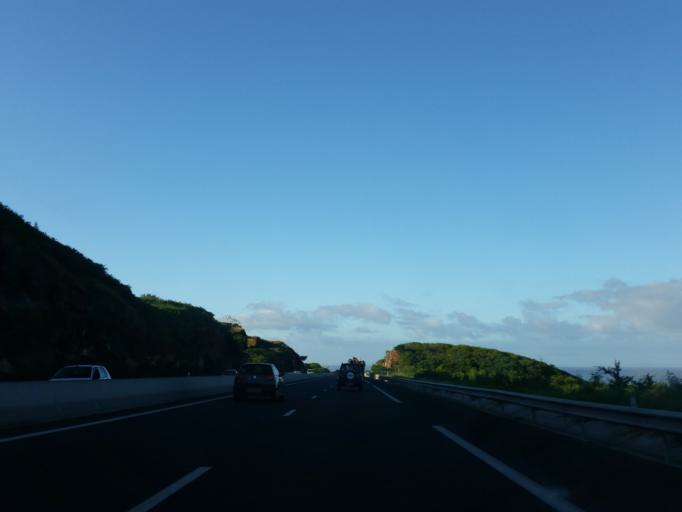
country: RE
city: Piton Saint-Leu
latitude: -21.2341
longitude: 55.3127
